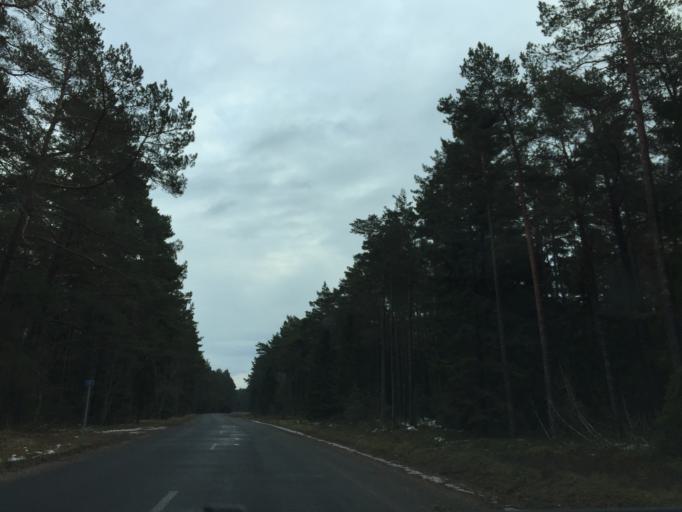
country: EE
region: Saare
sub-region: Kuressaare linn
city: Kuressaare
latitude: 58.4383
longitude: 22.0608
